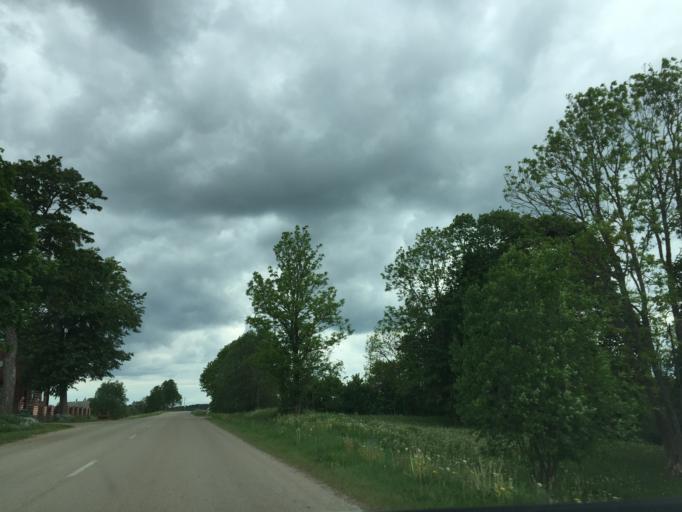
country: LV
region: Dagda
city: Dagda
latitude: 56.1053
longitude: 27.4962
